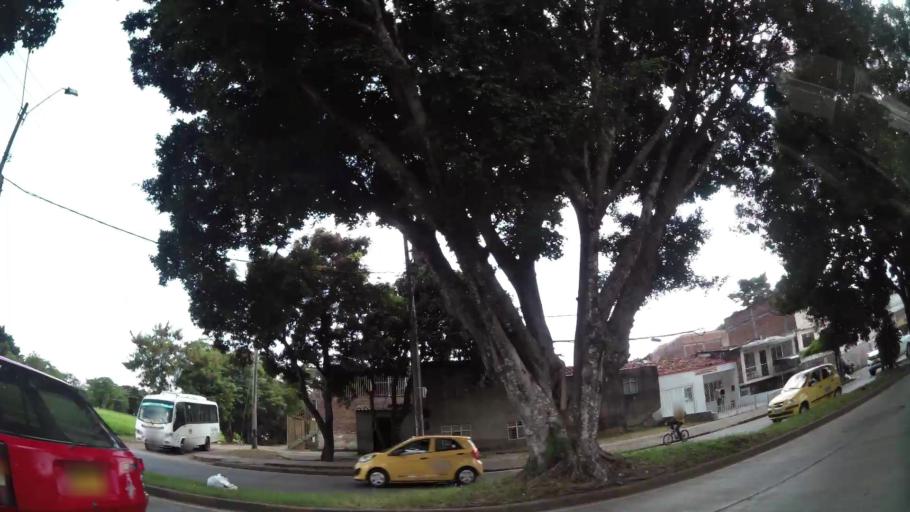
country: CO
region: Valle del Cauca
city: Cali
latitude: 3.4117
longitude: -76.5223
